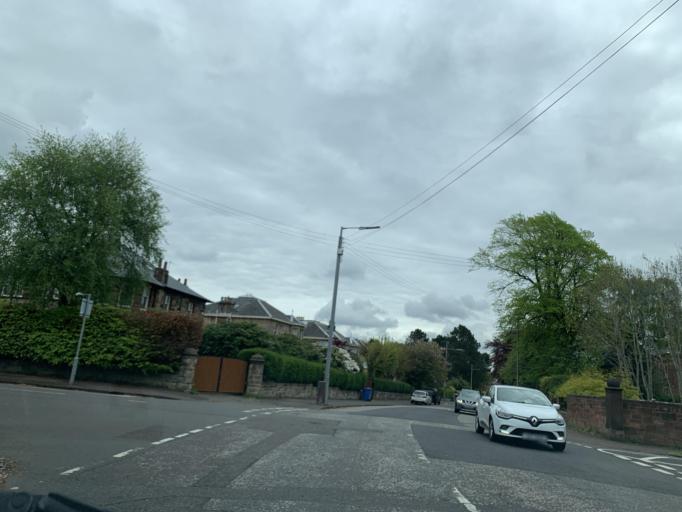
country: GB
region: Scotland
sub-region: East Renfrewshire
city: Giffnock
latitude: 55.8204
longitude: -4.2809
